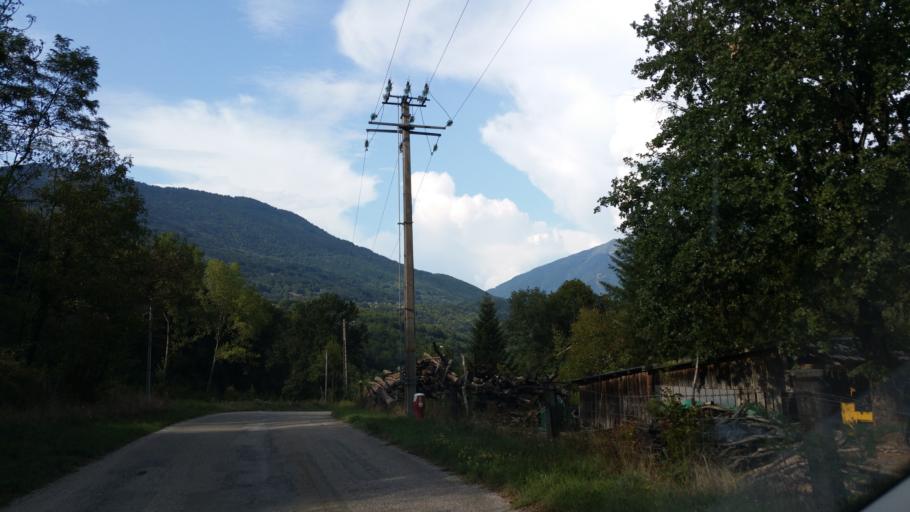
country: FR
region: Rhone-Alpes
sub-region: Departement de la Savoie
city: Saint-Remy-de-Maurienne
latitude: 45.4746
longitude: 6.2806
